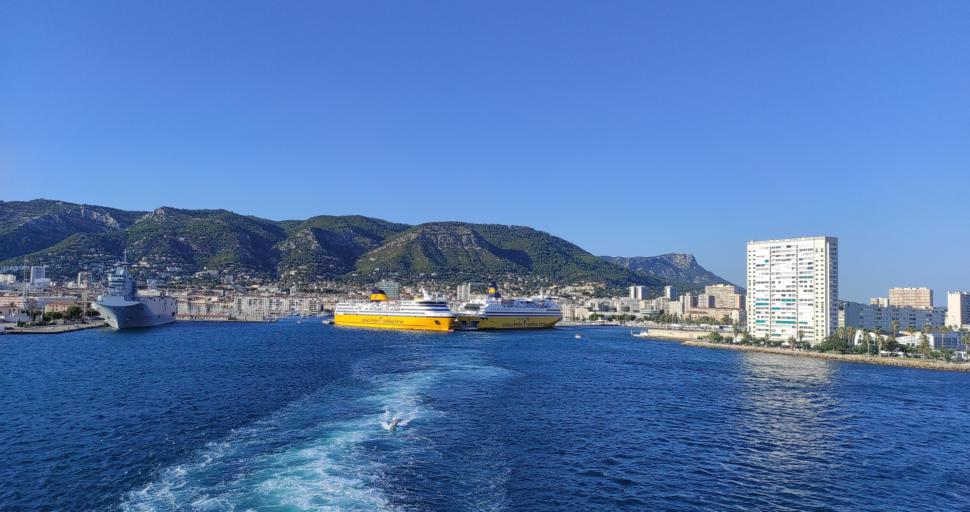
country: FR
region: Provence-Alpes-Cote d'Azur
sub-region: Departement du Var
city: Toulon
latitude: 43.1112
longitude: 5.9262
